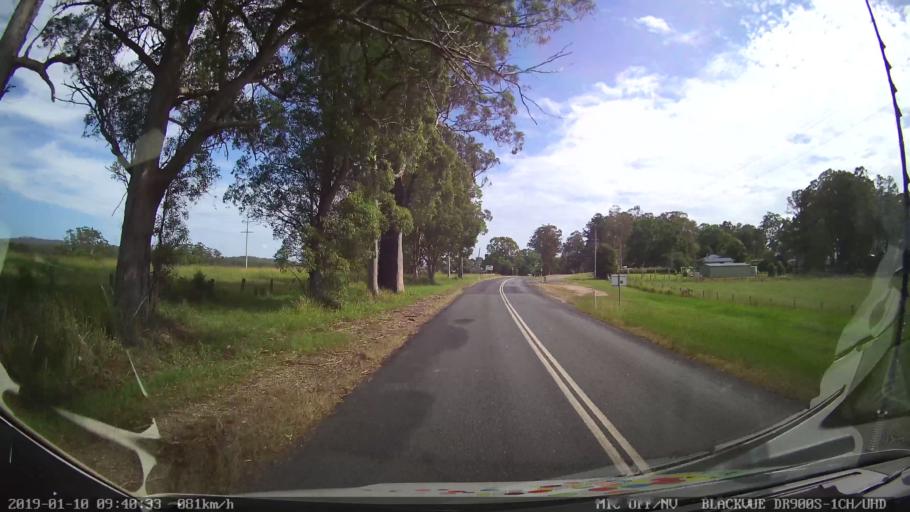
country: AU
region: New South Wales
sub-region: Coffs Harbour
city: Nana Glen
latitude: -30.1504
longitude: 153.0047
